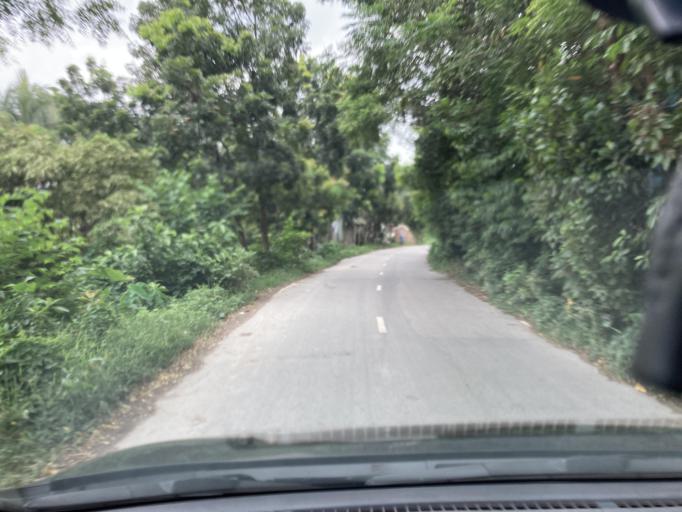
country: BD
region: Dhaka
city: Azimpur
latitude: 23.7814
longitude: 90.2120
